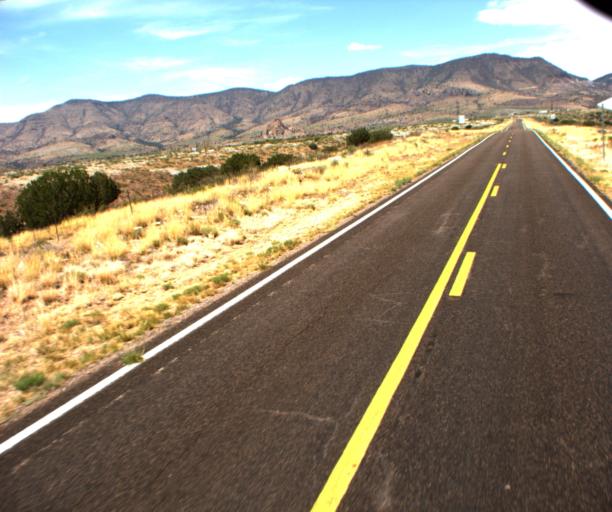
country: US
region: Arizona
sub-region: Greenlee County
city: Clifton
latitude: 33.0299
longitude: -109.1421
